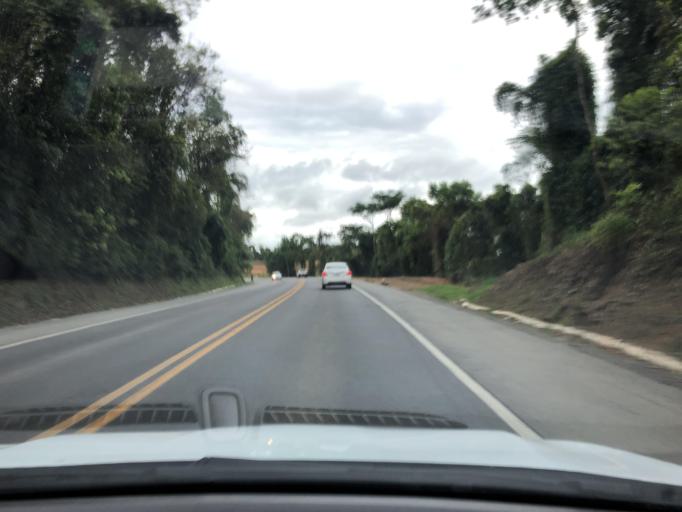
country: BR
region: Santa Catarina
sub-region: Joinville
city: Joinville
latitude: -26.4213
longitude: -48.7801
